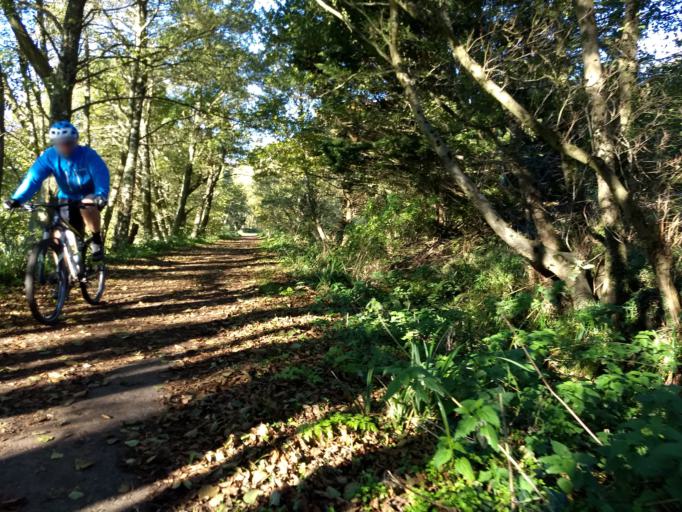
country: GB
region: England
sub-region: Isle of Wight
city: Newport
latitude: 50.6777
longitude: -1.2878
